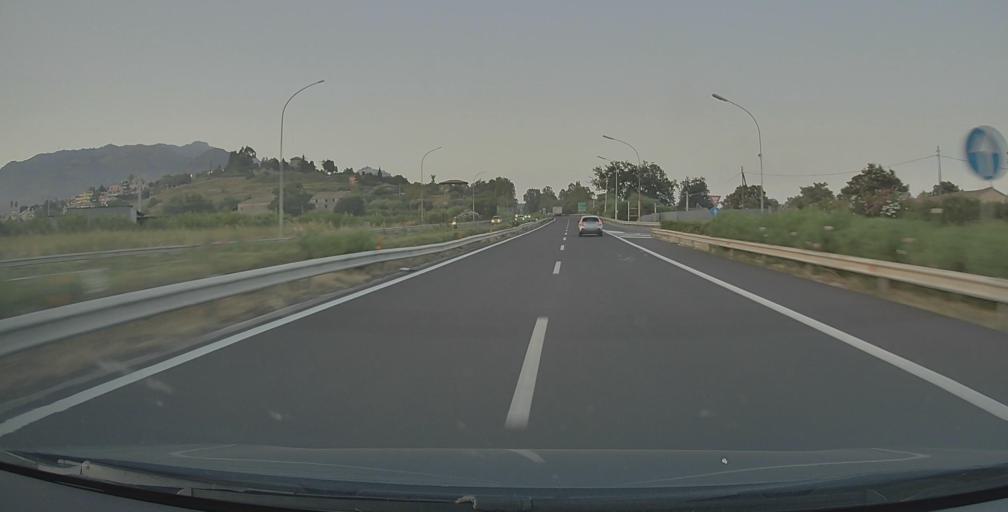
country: IT
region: Sicily
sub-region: Messina
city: Chianchitta-Trappitello
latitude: 37.8248
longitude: 15.2467
